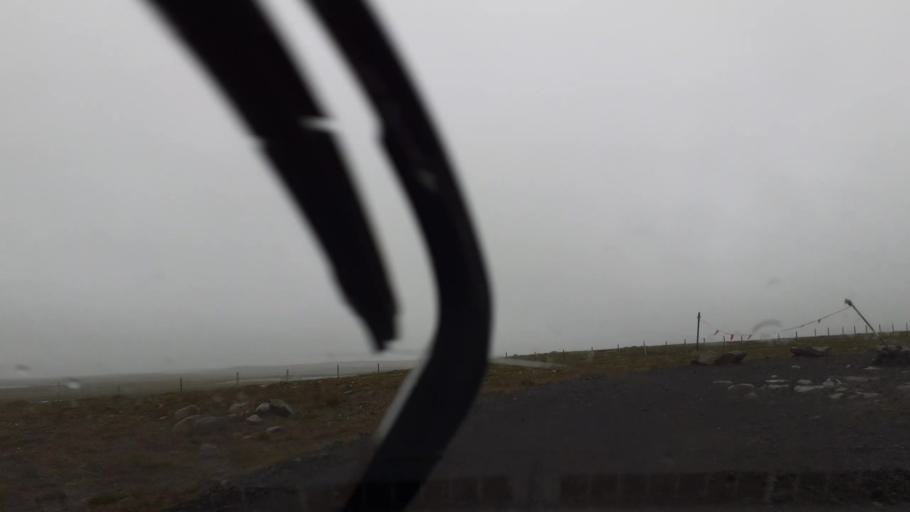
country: IS
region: Northeast
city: Husavik
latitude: 66.4600
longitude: -15.9651
